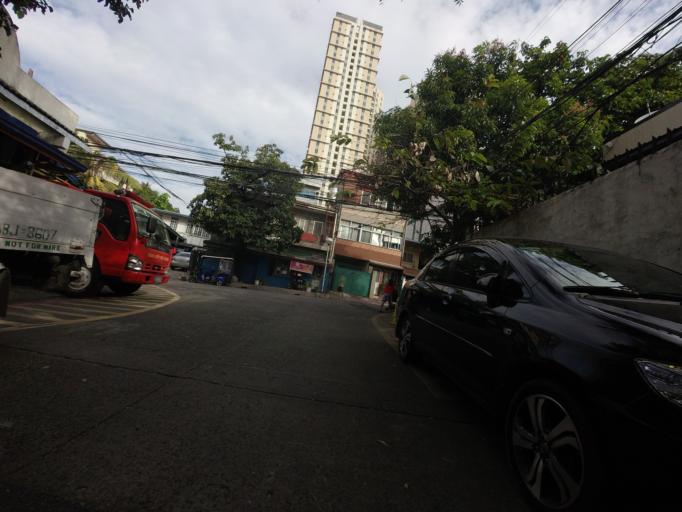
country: PH
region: Metro Manila
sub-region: Pasig
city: Pasig City
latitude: 14.5717
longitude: 121.0597
